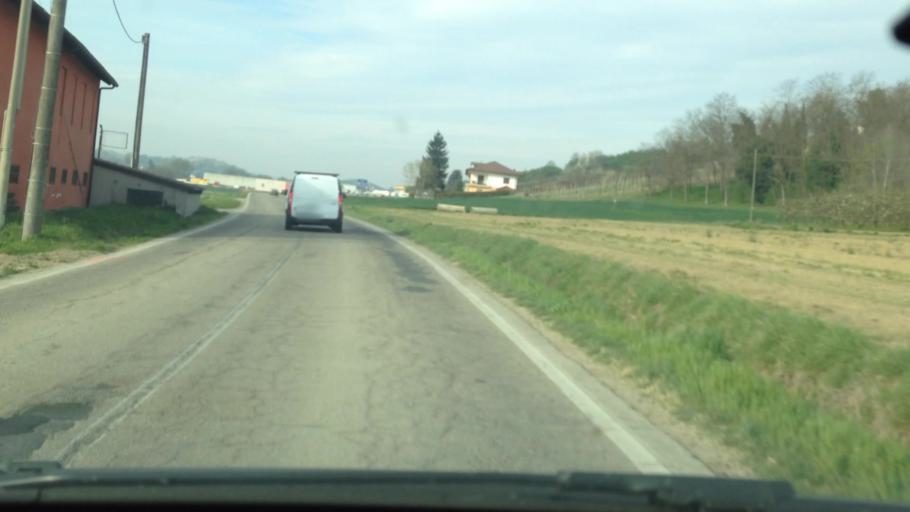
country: IT
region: Piedmont
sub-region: Provincia di Asti
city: San Damiano d'Asti
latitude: 44.8102
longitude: 8.0379
